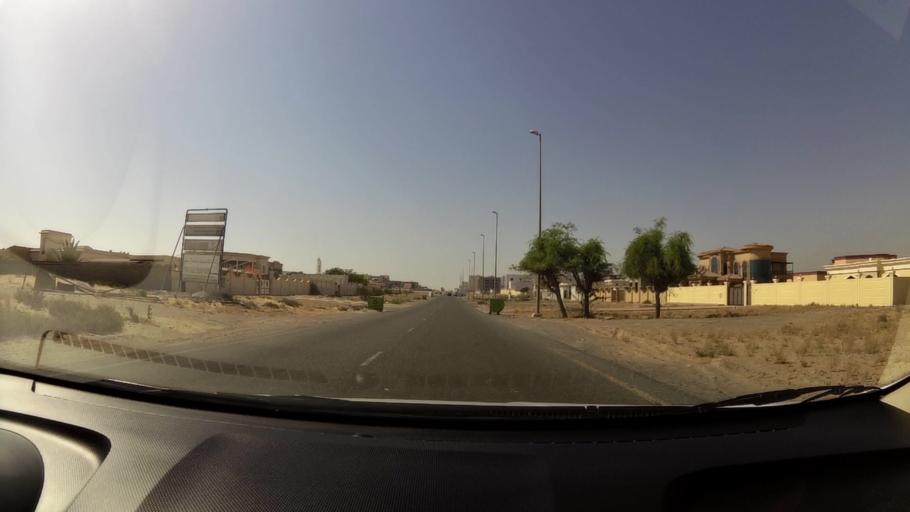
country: AE
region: Umm al Qaywayn
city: Umm al Qaywayn
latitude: 25.4883
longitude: 55.6010
